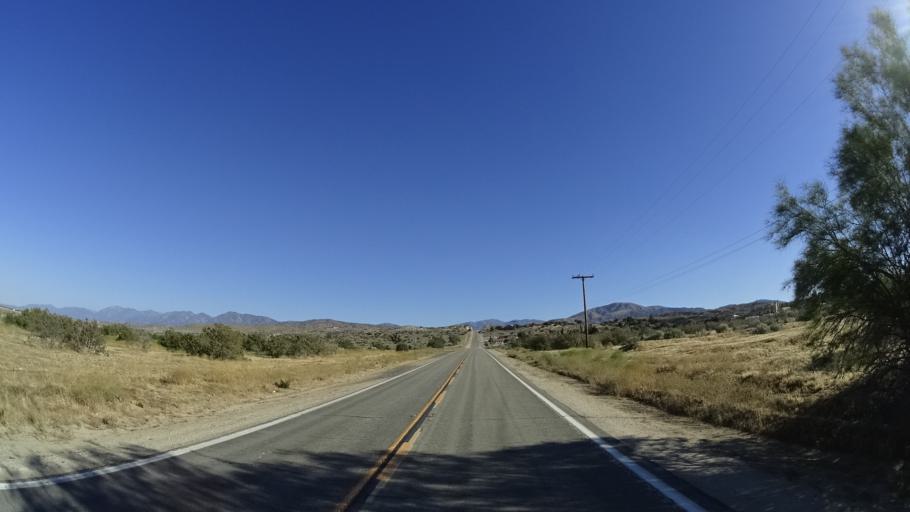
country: US
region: California
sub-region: Los Angeles County
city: Littlerock
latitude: 34.5355
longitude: -118.0277
